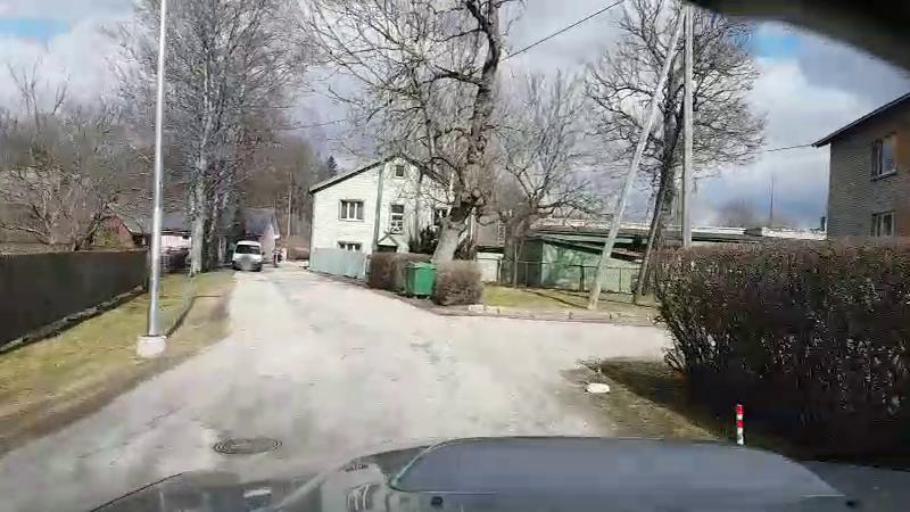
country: EE
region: Jaervamaa
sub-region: Paide linn
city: Paide
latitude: 58.8872
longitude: 25.5749
